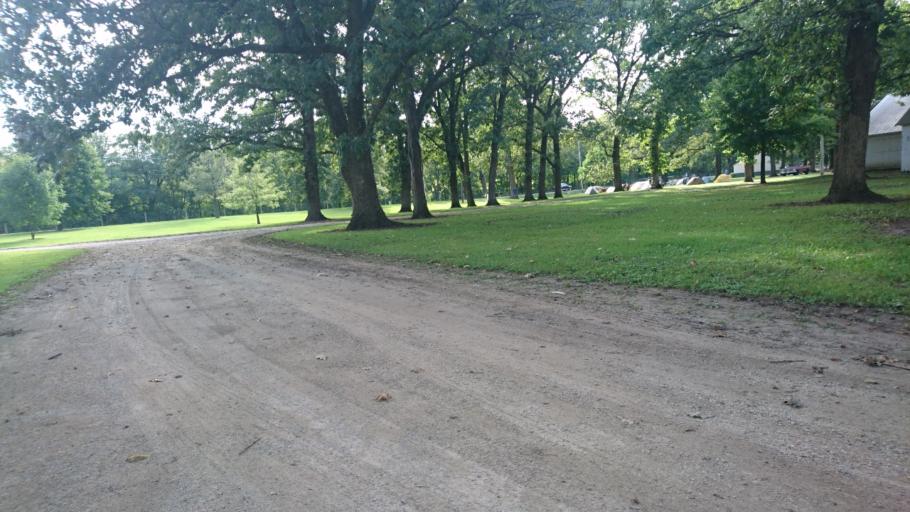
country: US
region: Illinois
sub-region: Livingston County
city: Pontiac
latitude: 40.8912
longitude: -88.6629
